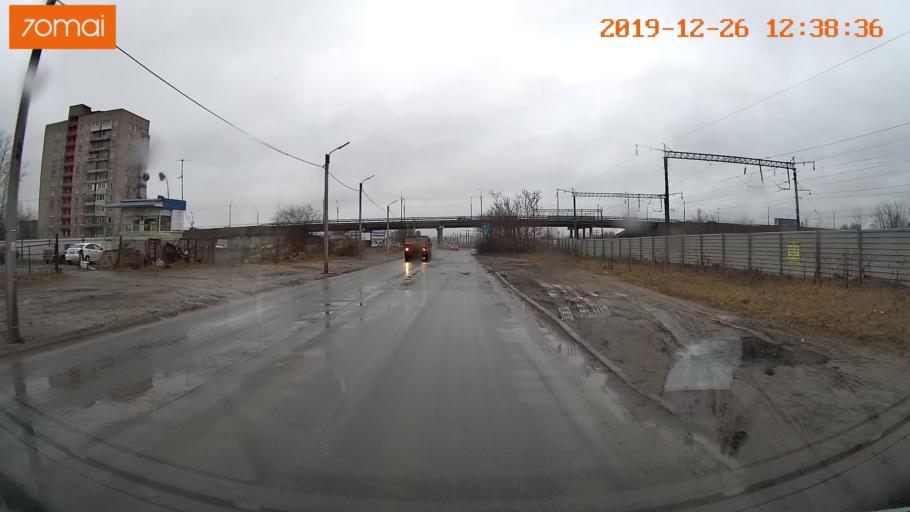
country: RU
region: Vologda
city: Tonshalovo
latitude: 59.1367
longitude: 37.9801
